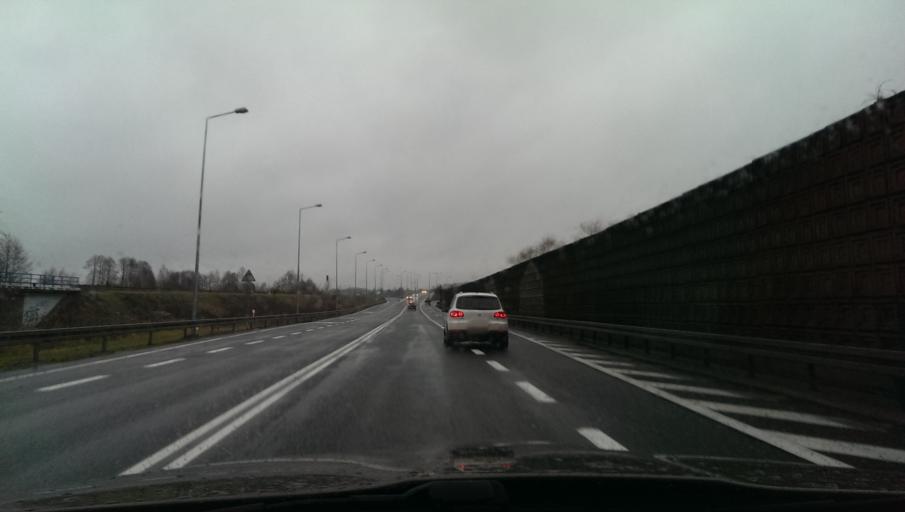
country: PL
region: Subcarpathian Voivodeship
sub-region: Powiat rzeszowski
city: Glogow Malopolski
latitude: 50.1383
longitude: 21.9650
